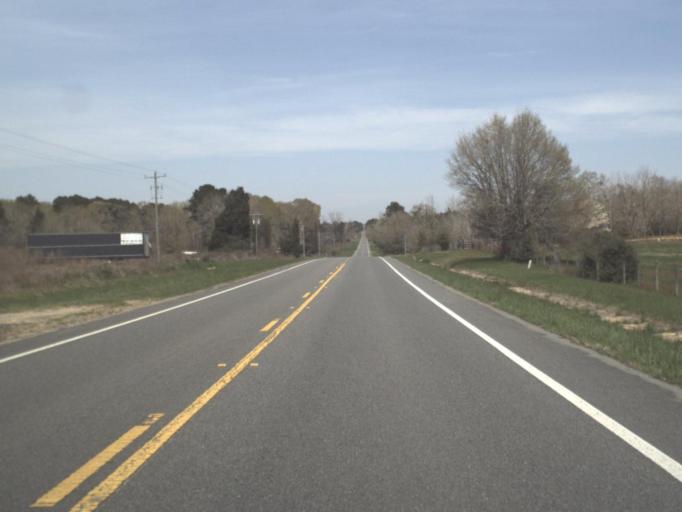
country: US
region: Florida
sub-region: Walton County
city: DeFuniak Springs
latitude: 30.7649
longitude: -85.9589
